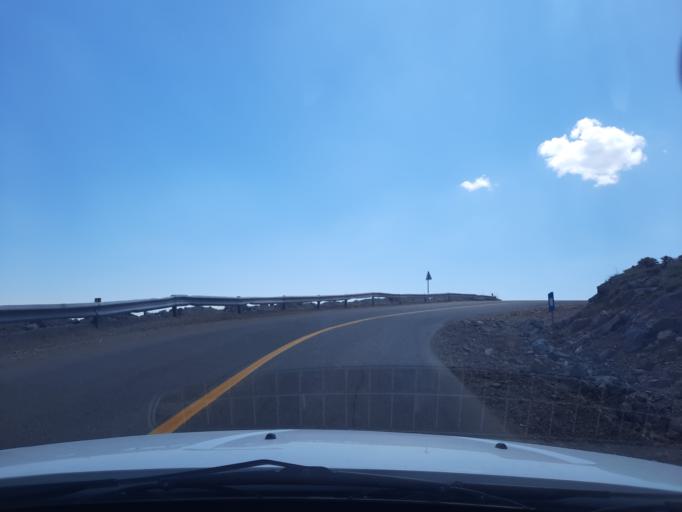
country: IR
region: Qazvin
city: Qazvin
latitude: 36.3803
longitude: 50.2030
